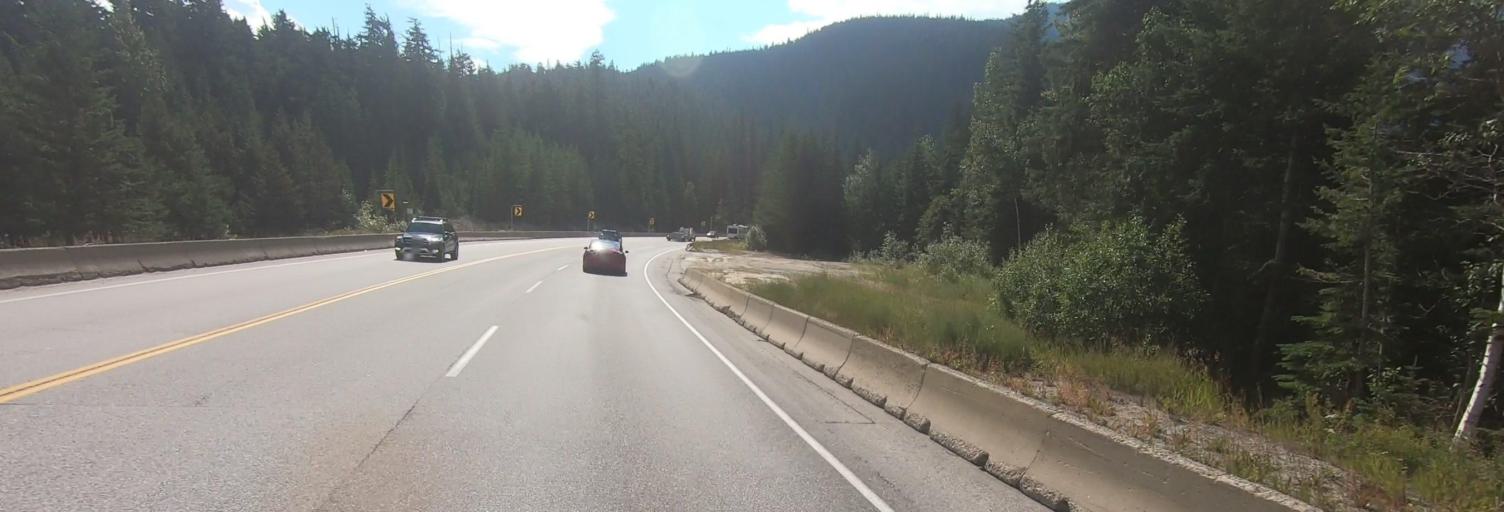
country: CA
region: British Columbia
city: Golden
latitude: 51.3472
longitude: -117.4349
